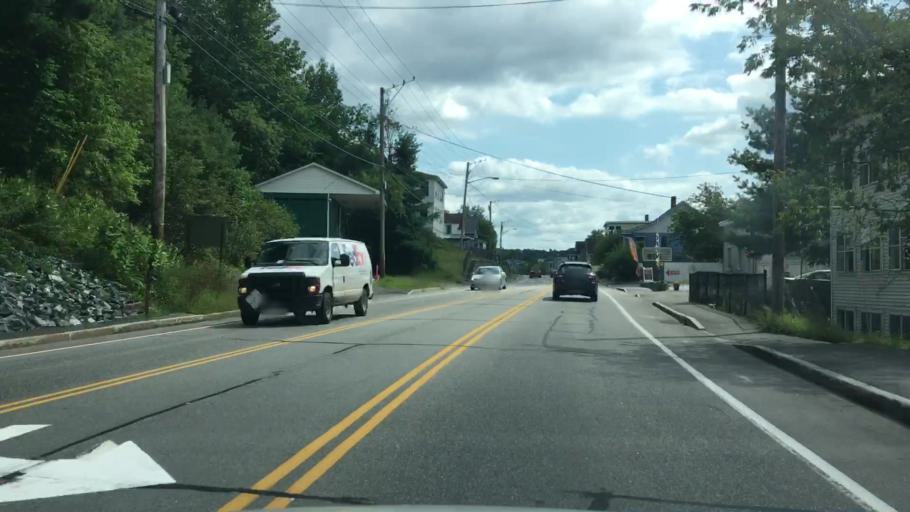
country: US
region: Maine
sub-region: Kennebec County
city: Augusta
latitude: 44.3266
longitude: -69.7785
